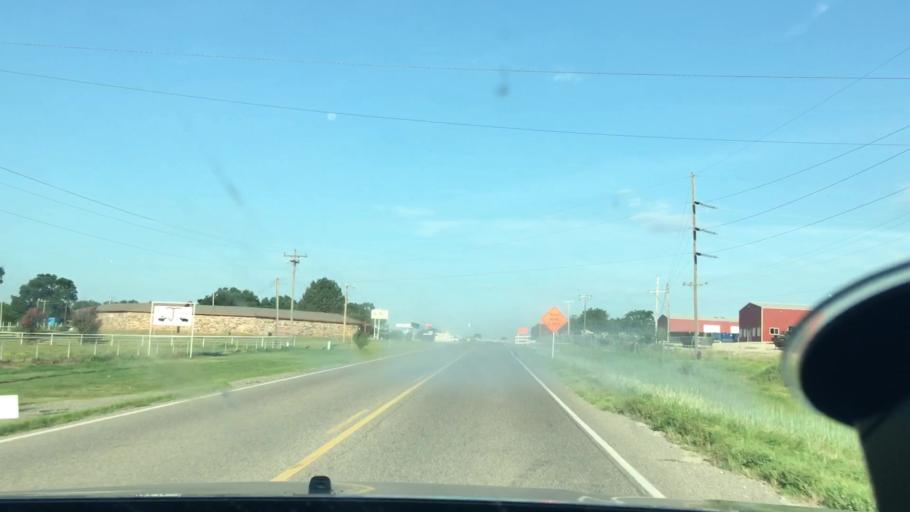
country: US
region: Oklahoma
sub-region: Garvin County
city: Wynnewood
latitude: 34.6517
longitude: -97.2117
